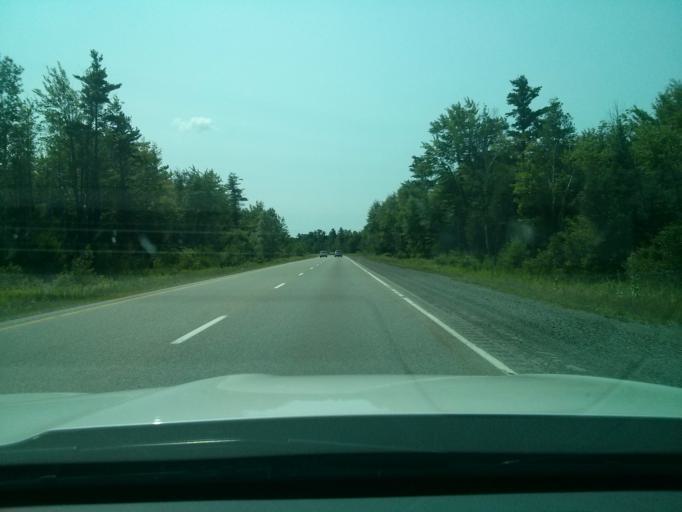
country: CA
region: Ontario
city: Prescott
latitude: 44.7967
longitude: -75.5139
